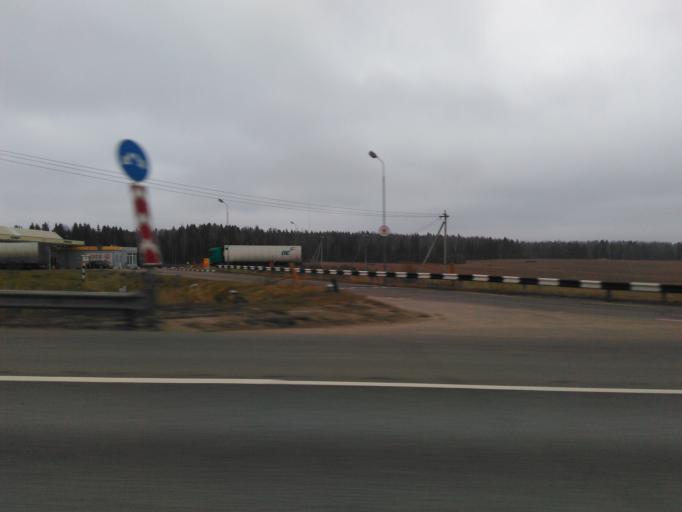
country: RU
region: Moskovskaya
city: Lesnoy
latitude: 56.0553
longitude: 37.8985
